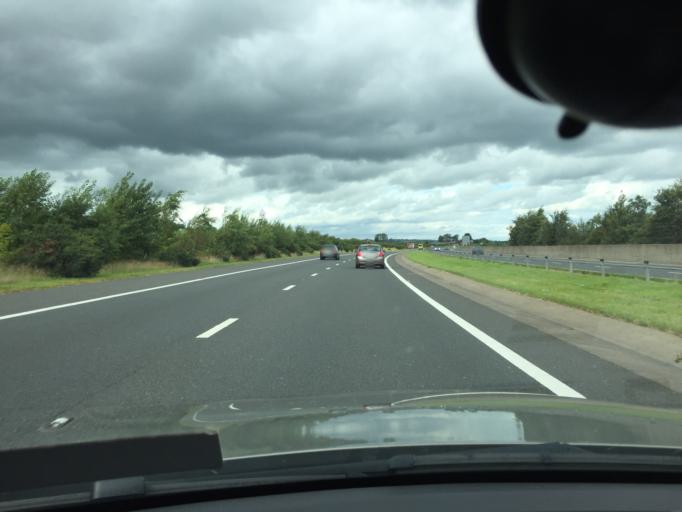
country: GB
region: Northern Ireland
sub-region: Newry and Mourne District
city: Newry
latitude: 54.1620
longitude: -6.3591
